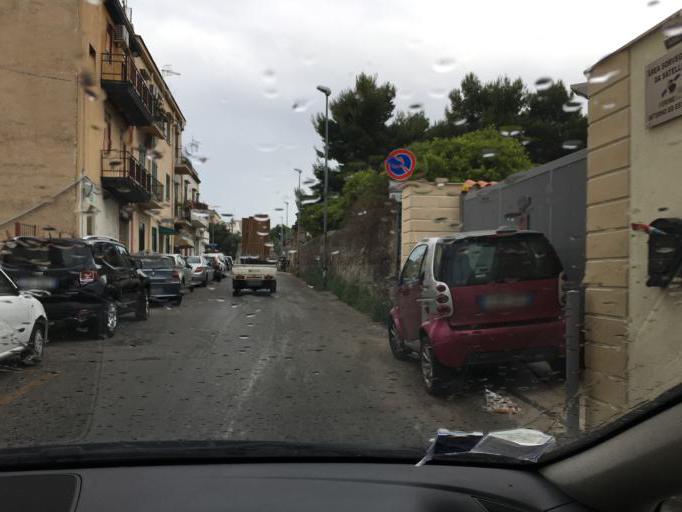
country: IT
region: Sicily
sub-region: Palermo
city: Isola delle Femmine
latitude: 38.1968
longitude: 13.3141
